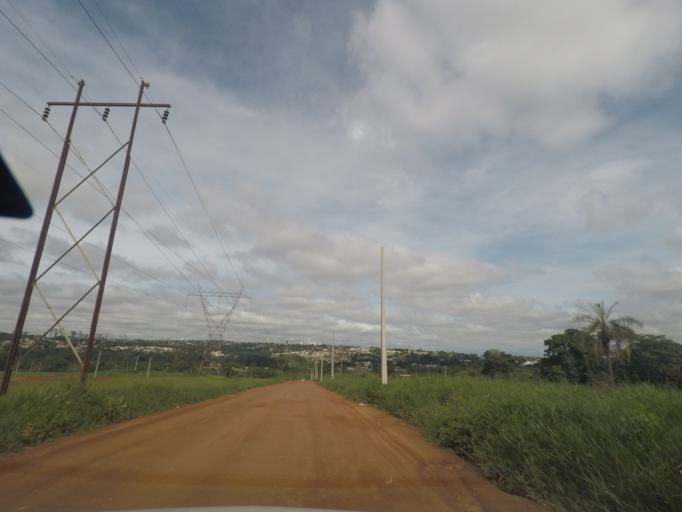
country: BR
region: Goias
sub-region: Goiania
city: Goiania
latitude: -16.6750
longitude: -49.1925
